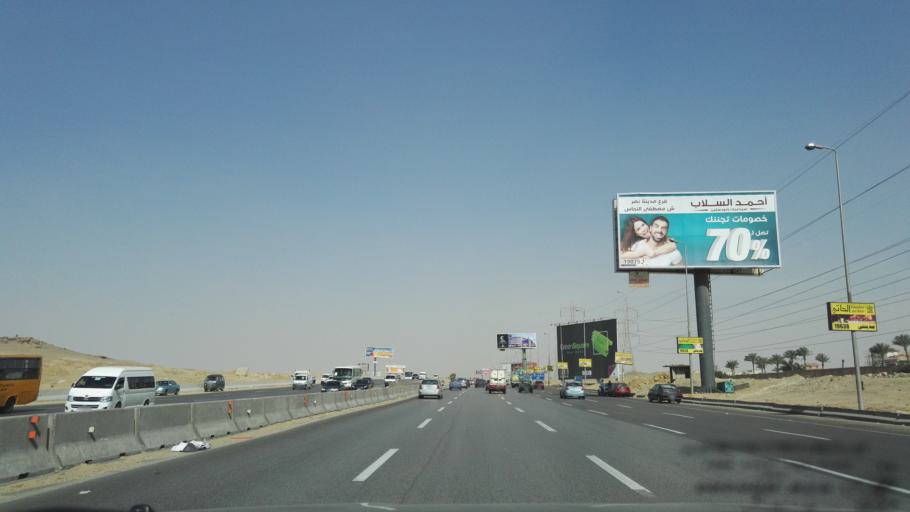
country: EG
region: Muhafazat al Qalyubiyah
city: Al Khankah
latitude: 30.0802
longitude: 31.4430
